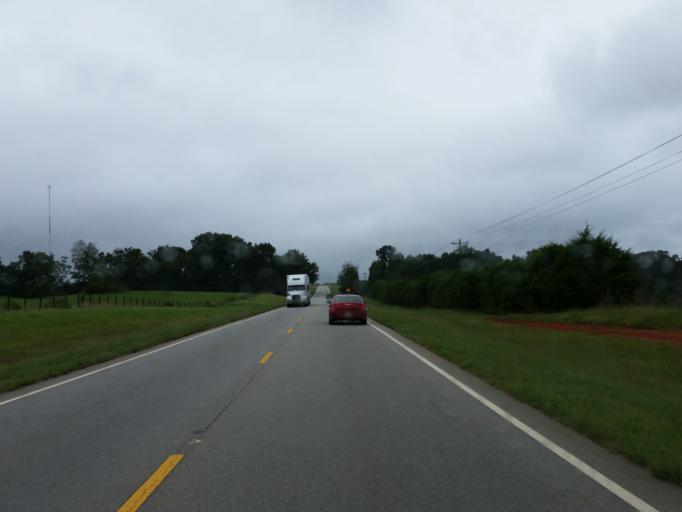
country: US
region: Georgia
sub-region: Crawford County
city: Roberta
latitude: 32.8858
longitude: -84.0874
